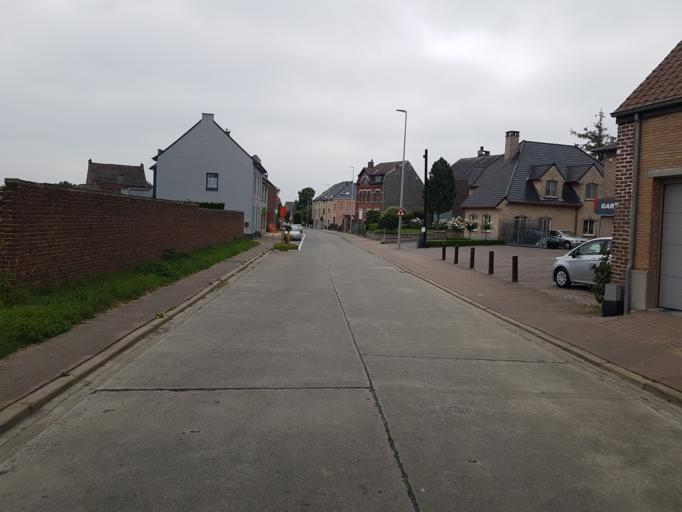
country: BE
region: Flanders
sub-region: Provincie Oost-Vlaanderen
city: Denderleeuw
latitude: 50.8764
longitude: 4.0430
